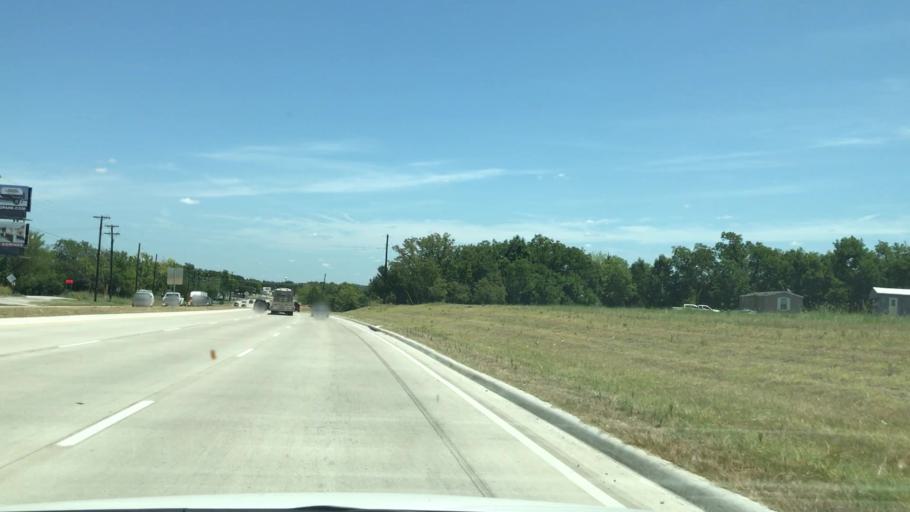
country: US
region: Texas
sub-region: Collin County
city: Wylie
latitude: 33.0236
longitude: -96.4939
